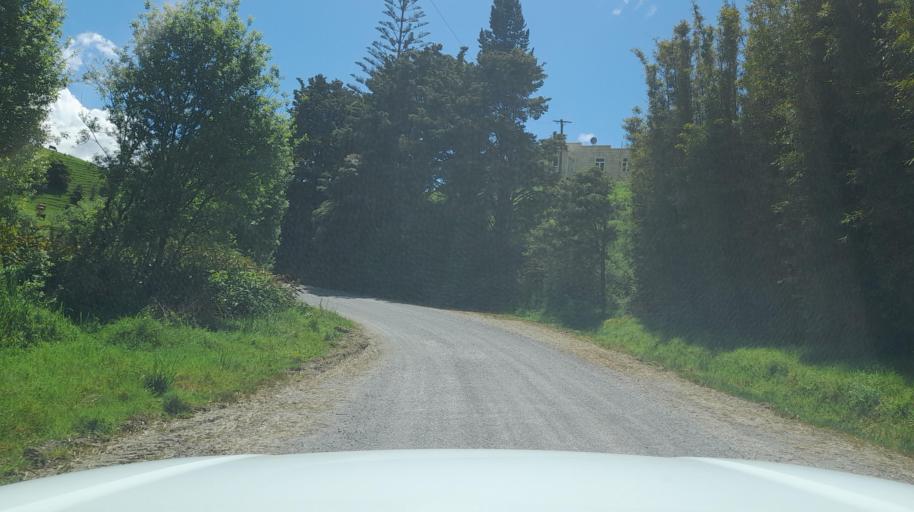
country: NZ
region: Northland
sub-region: Far North District
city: Taipa
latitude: -35.1227
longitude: 173.4077
